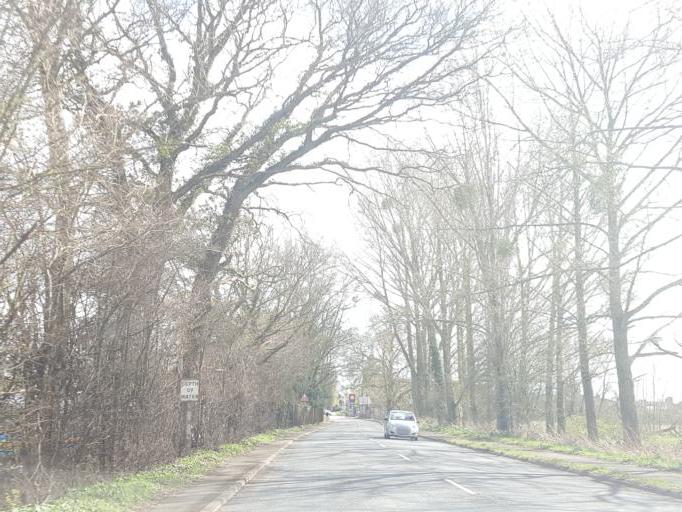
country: GB
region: England
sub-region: Worcestershire
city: Upton upon Severn
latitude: 52.0669
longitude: -2.2233
